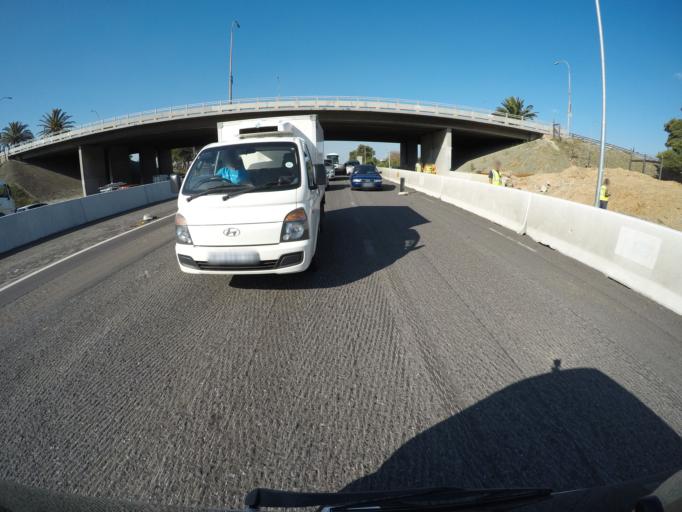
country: ZA
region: Western Cape
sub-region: City of Cape Town
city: Kraaifontein
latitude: -33.8826
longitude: 18.6459
